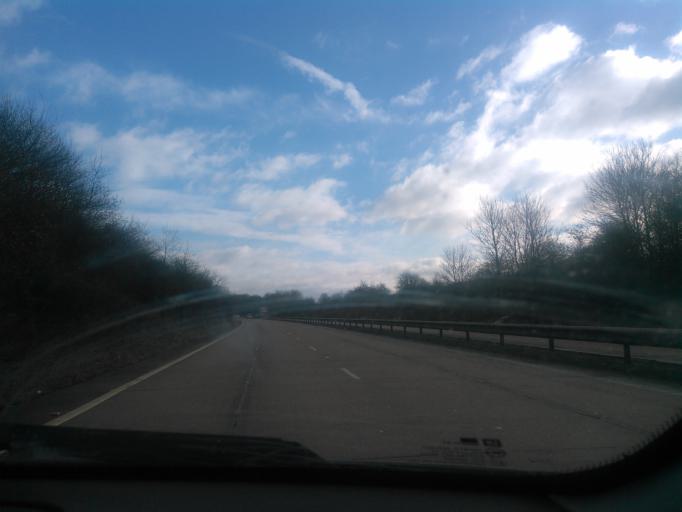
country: GB
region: England
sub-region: Staffordshire
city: Cheadle
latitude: 52.9573
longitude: -2.0458
